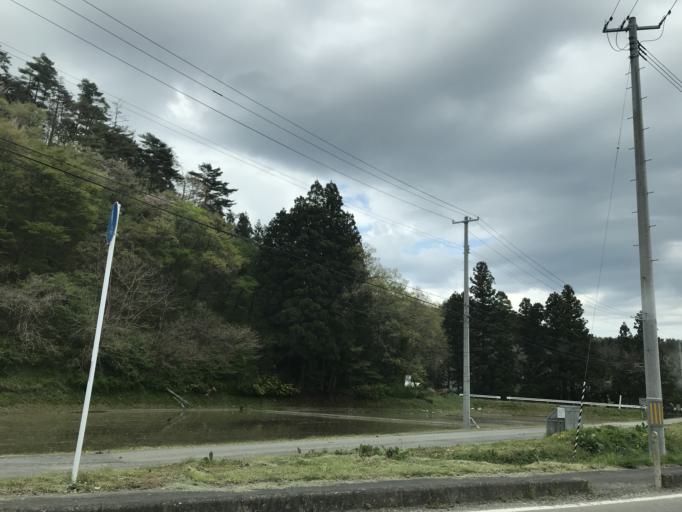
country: JP
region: Iwate
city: Ichinoseki
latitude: 38.7839
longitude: 141.3257
